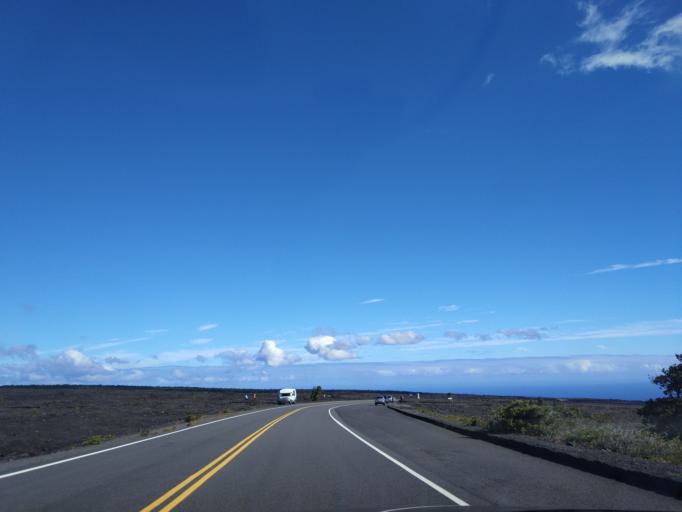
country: US
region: Hawaii
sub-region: Hawaii County
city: Volcano
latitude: 19.3372
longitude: -155.2050
